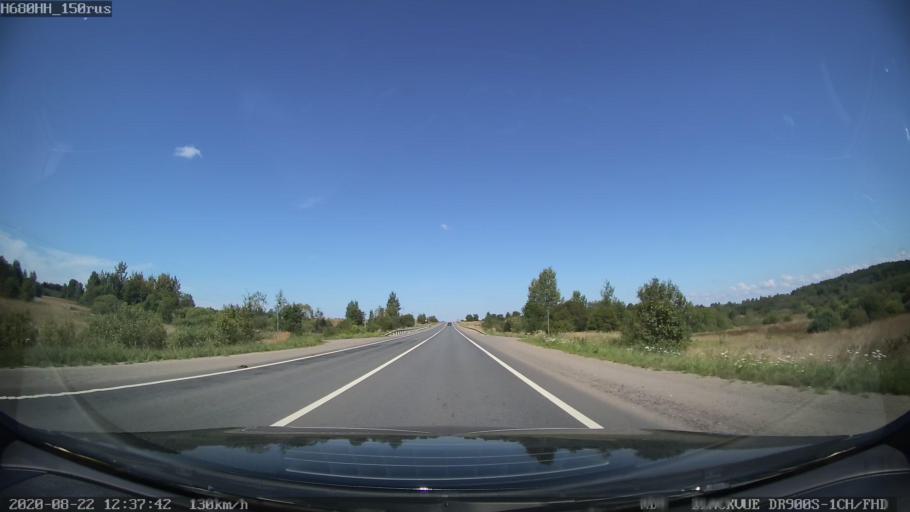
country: RU
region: Tverskaya
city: Rameshki
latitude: 57.3007
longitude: 36.0889
